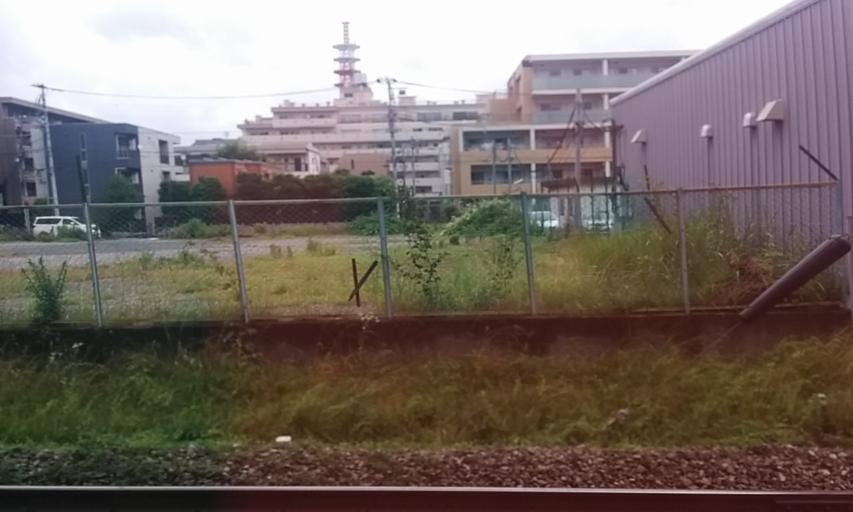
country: JP
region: Tokyo
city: Hachioji
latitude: 35.6549
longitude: 139.3470
